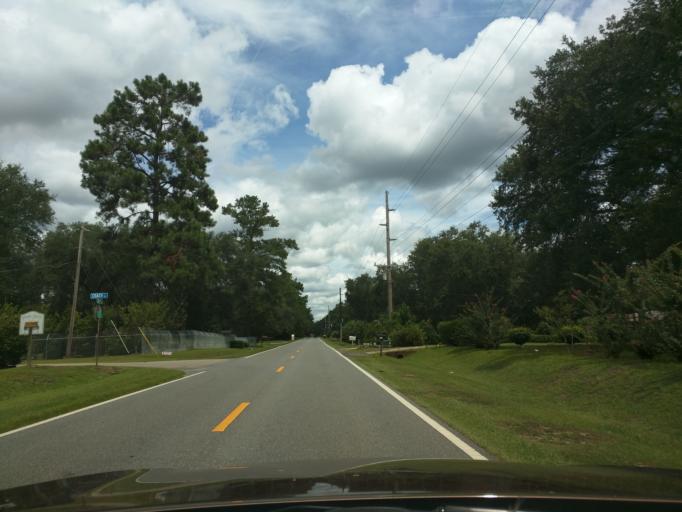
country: US
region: Florida
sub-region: Leon County
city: Tallahassee
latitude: 30.5222
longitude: -84.1299
